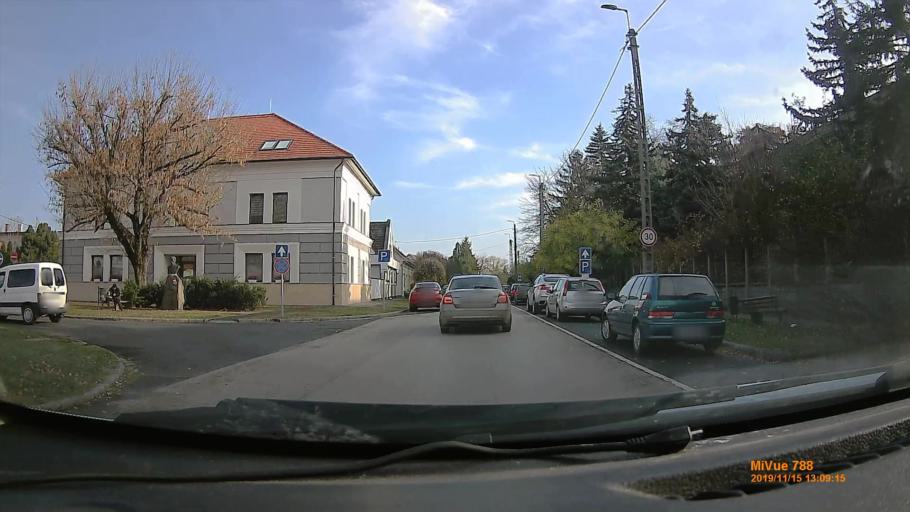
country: HU
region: Bekes
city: Gyula
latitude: 46.6425
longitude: 21.2763
